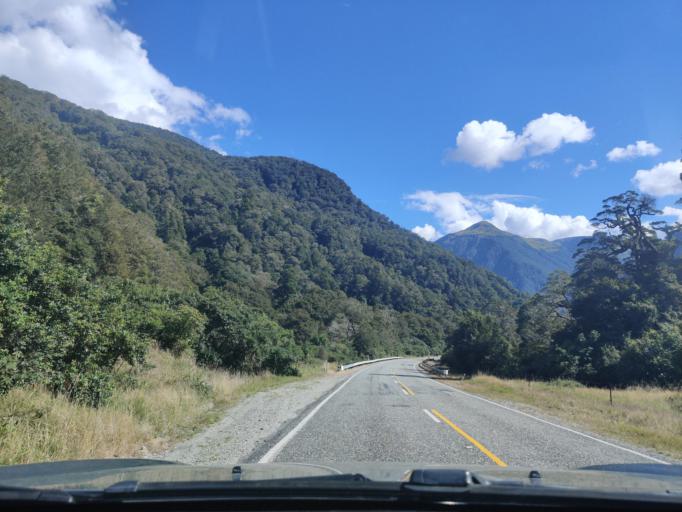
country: NZ
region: Otago
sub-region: Queenstown-Lakes District
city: Wanaka
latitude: -43.9668
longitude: 169.3753
